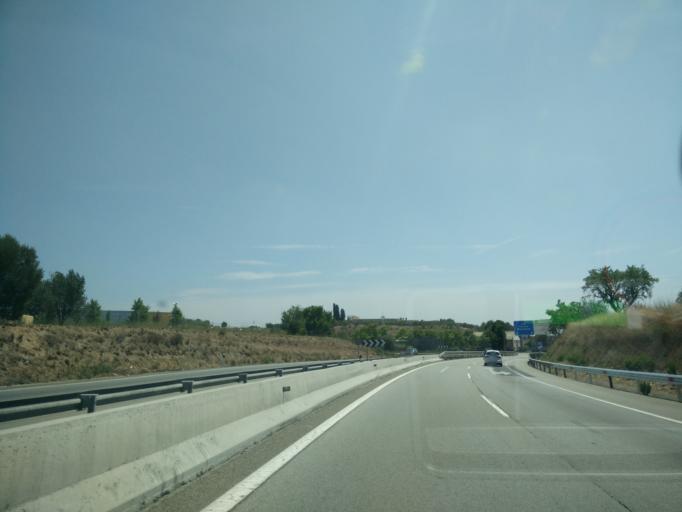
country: ES
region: Catalonia
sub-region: Provincia de Barcelona
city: Esparreguera
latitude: 41.5308
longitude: 1.8751
